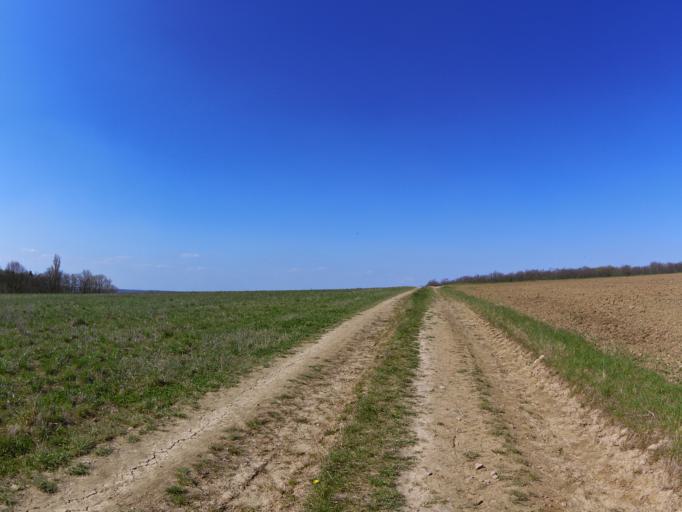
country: DE
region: Bavaria
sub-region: Regierungsbezirk Unterfranken
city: Kurnach
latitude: 49.8273
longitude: 10.0524
